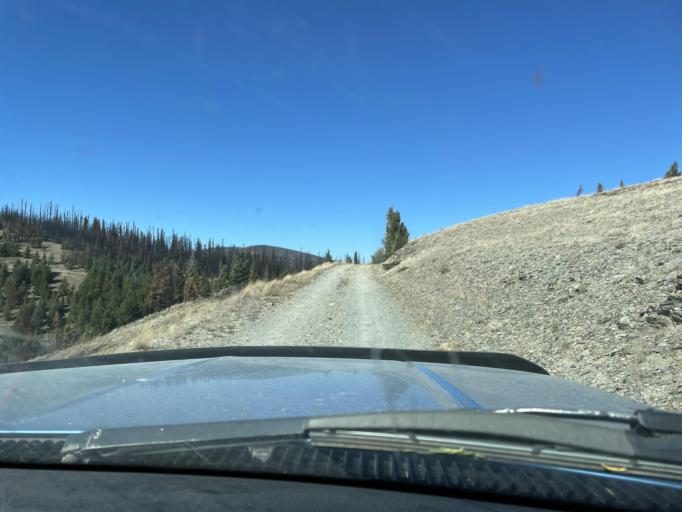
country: US
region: Montana
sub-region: Broadwater County
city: Townsend
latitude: 46.4965
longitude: -111.2571
